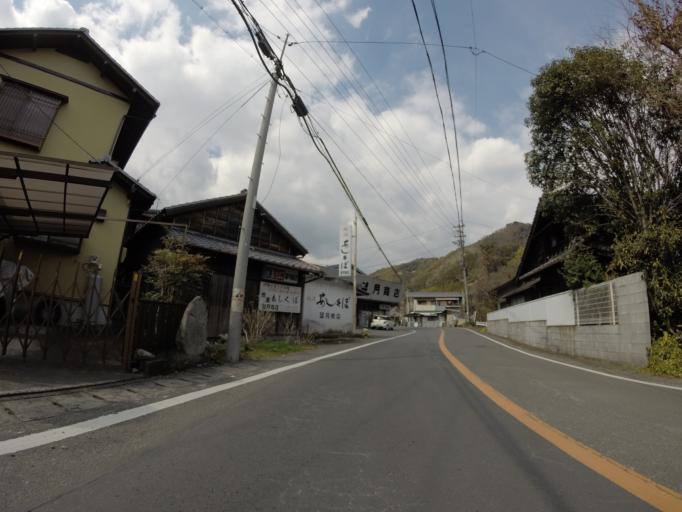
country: JP
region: Shizuoka
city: Shizuoka-shi
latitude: 35.0444
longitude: 138.3616
